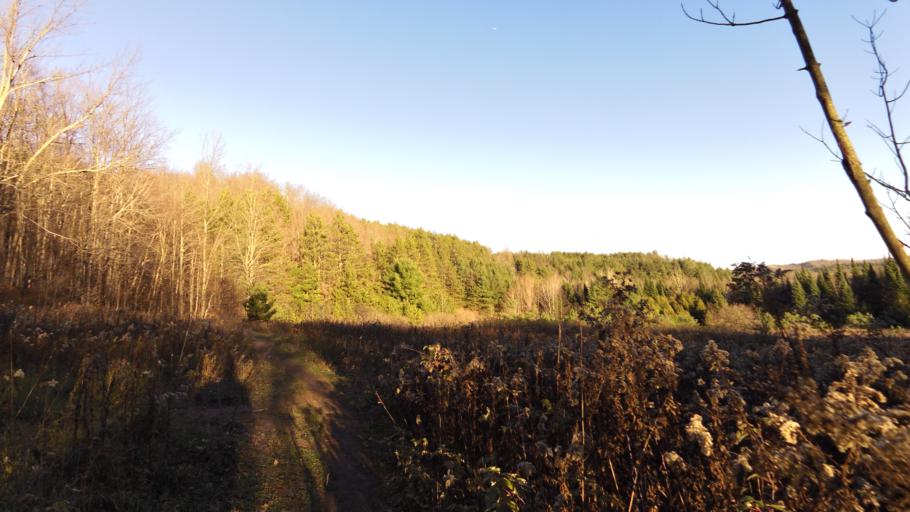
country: CA
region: Ontario
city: Orangeville
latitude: 43.9897
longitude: -80.0549
